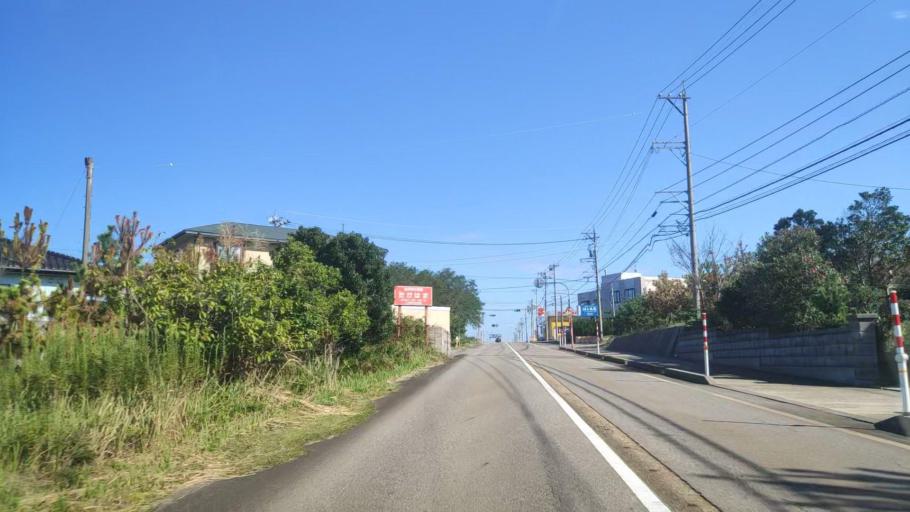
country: JP
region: Ishikawa
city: Hakui
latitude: 36.9868
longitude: 136.7758
